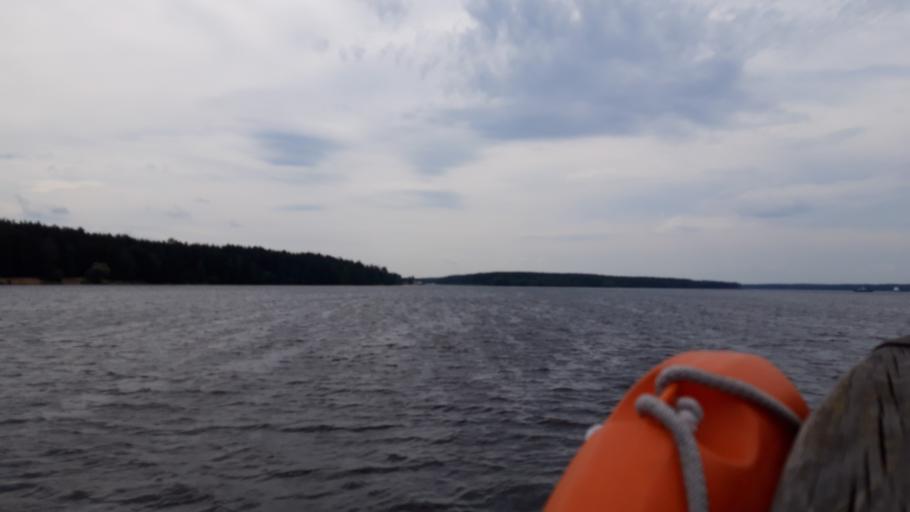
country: RU
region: Tverskaya
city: Konakovo
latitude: 56.7067
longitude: 36.7456
